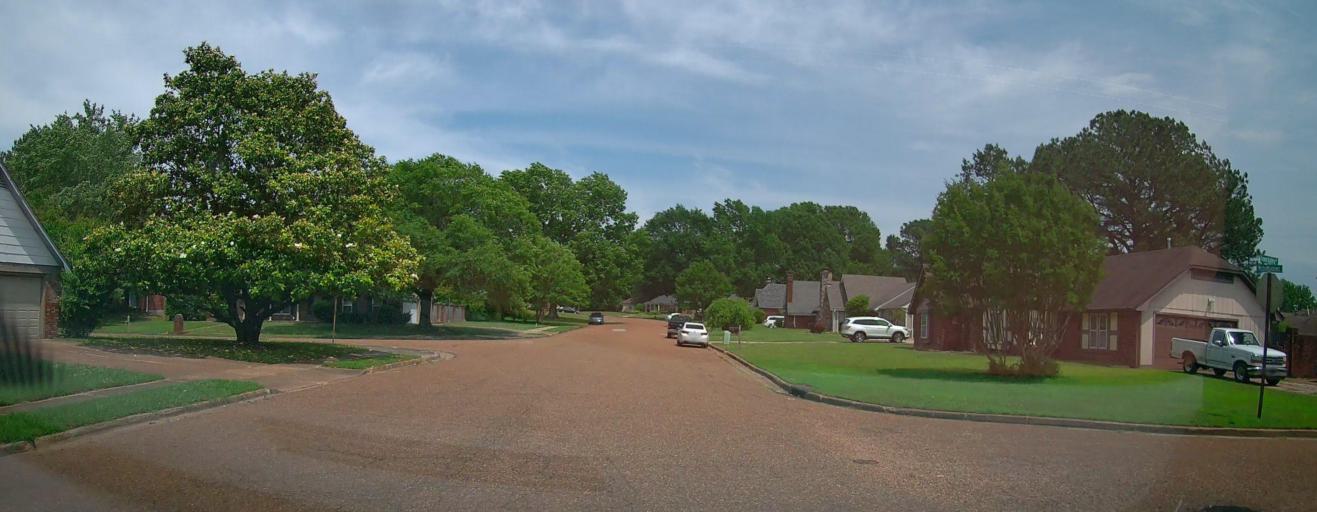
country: US
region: Tennessee
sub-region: Shelby County
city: Germantown
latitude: 35.0438
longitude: -89.7933
